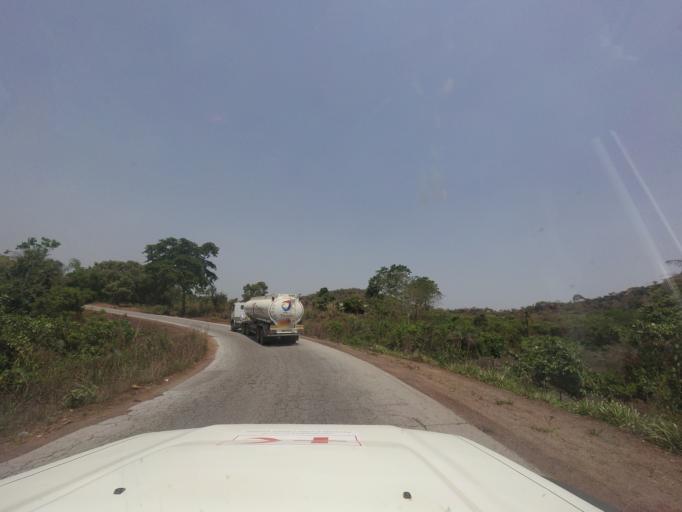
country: GN
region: Kindia
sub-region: Coyah
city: Coyah
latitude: 9.8354
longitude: -13.1387
